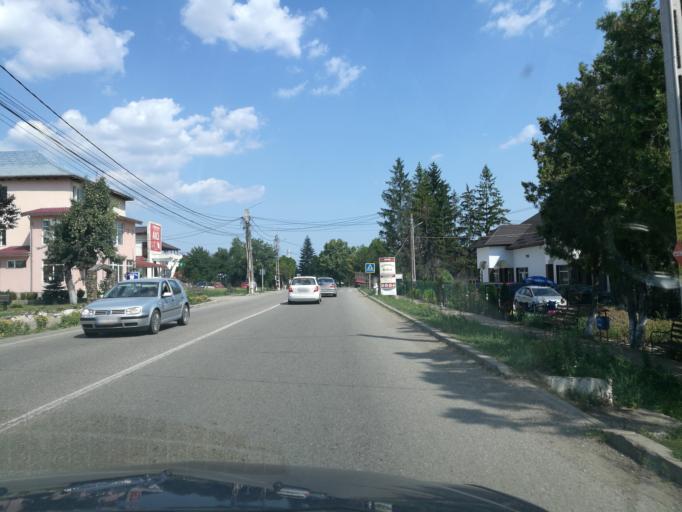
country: RO
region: Neamt
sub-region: Comuna Baltatesti
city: Baltatesti
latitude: 47.1210
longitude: 26.3097
